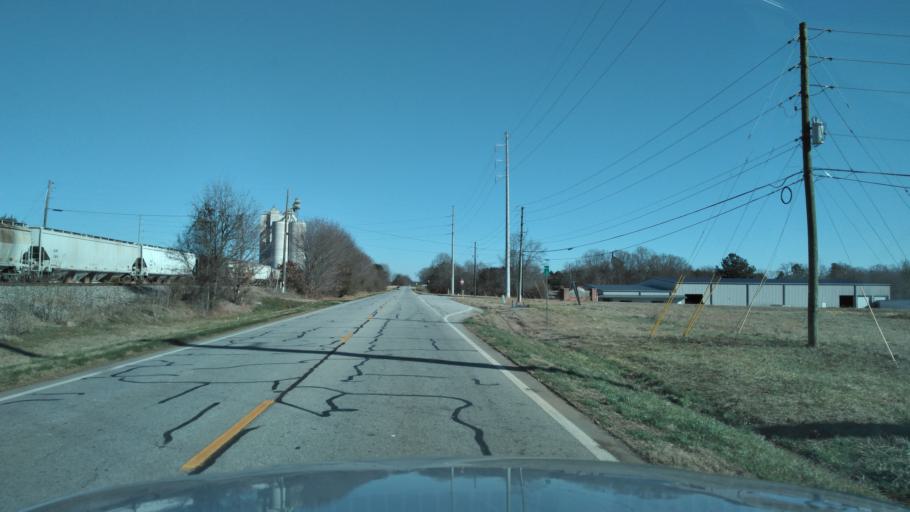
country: US
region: Georgia
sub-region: Banks County
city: Maysville
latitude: 34.2447
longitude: -83.5502
